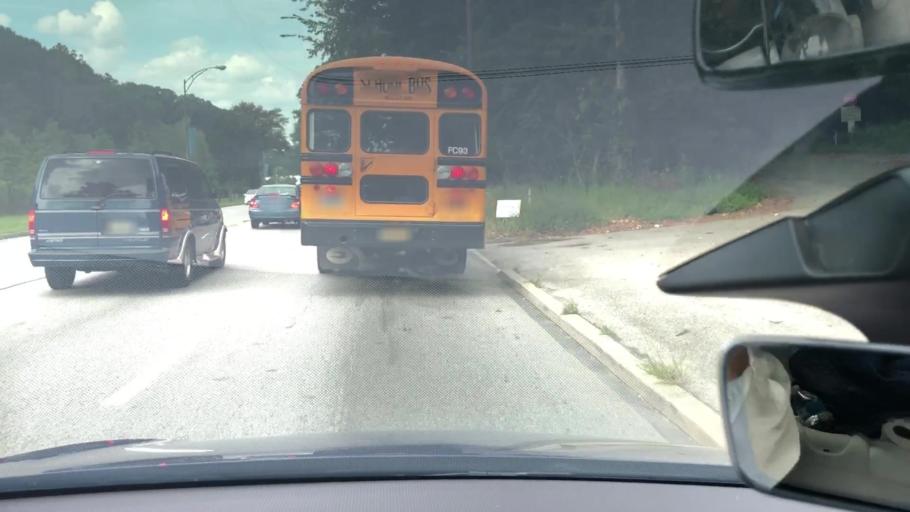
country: US
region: Pennsylvania
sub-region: Allegheny County
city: Aspinwall
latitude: 40.4794
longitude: -79.9079
